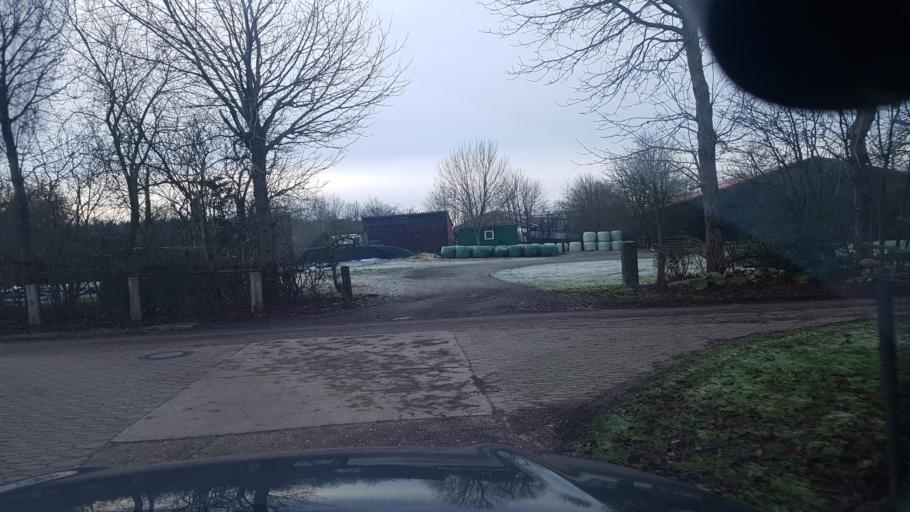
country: DE
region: Lower Saxony
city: Elmlohe
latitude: 53.6083
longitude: 8.6779
